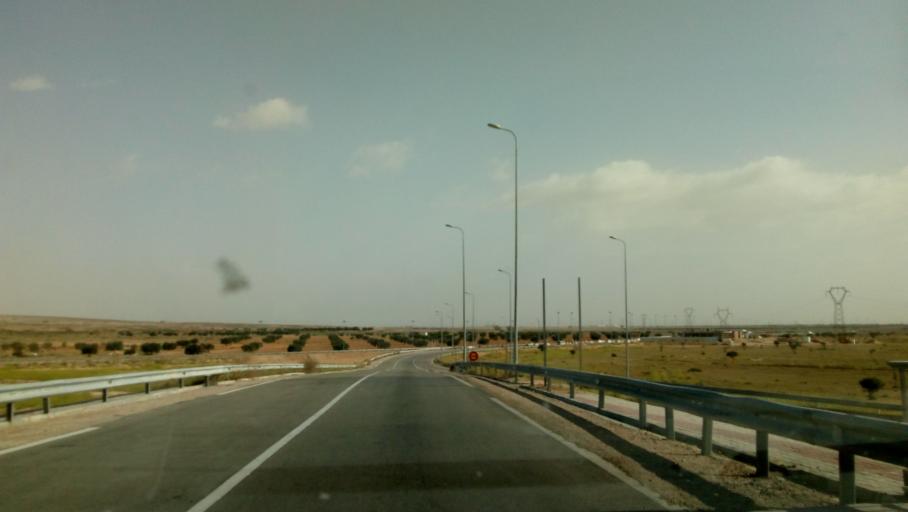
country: TN
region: Qabis
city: Gabes
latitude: 33.8816
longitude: 9.9964
